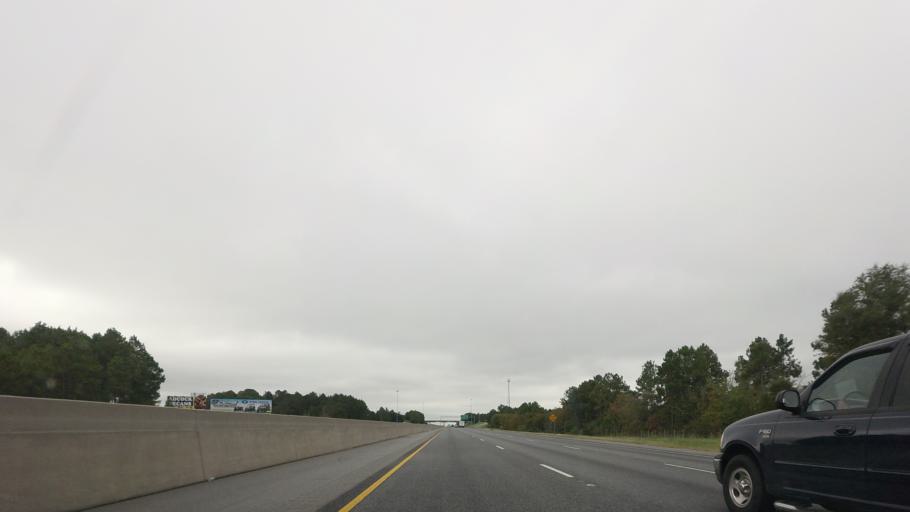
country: US
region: Georgia
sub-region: Tift County
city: Tifton
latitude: 31.5549
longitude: -83.5369
